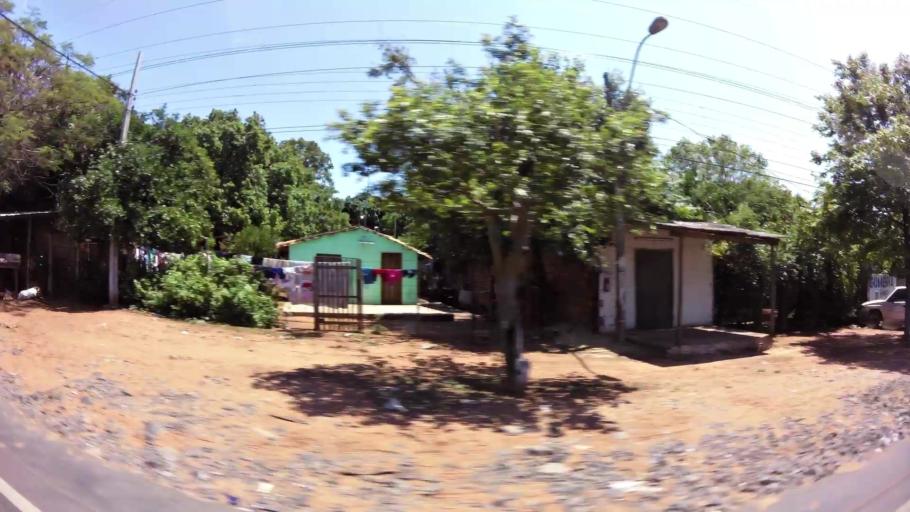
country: PY
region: Central
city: Nemby
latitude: -25.4067
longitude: -57.5445
